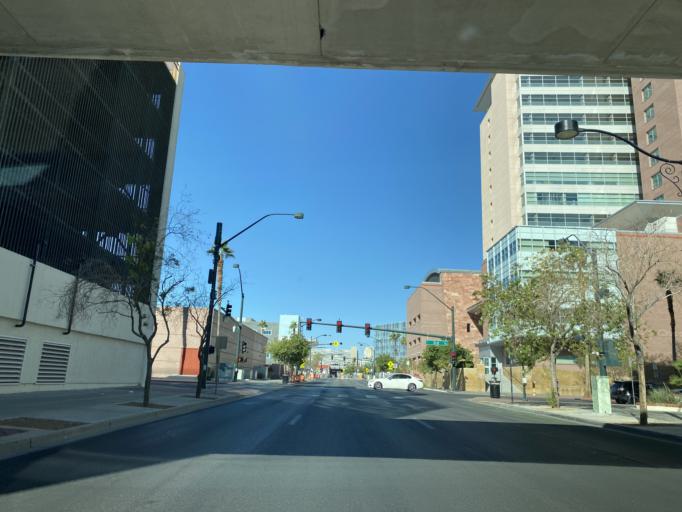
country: US
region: Nevada
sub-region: Clark County
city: Las Vegas
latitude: 36.1654
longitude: -115.1456
